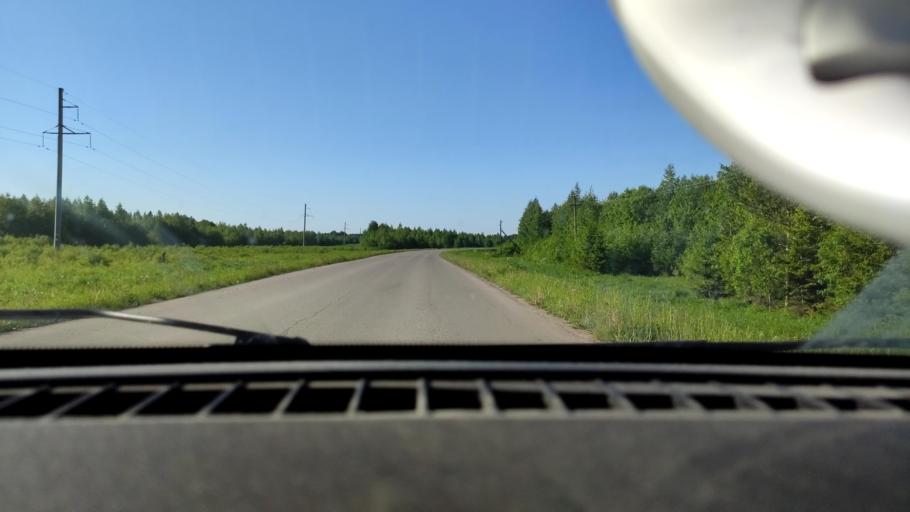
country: RU
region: Perm
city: Polazna
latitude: 58.2060
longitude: 56.5309
